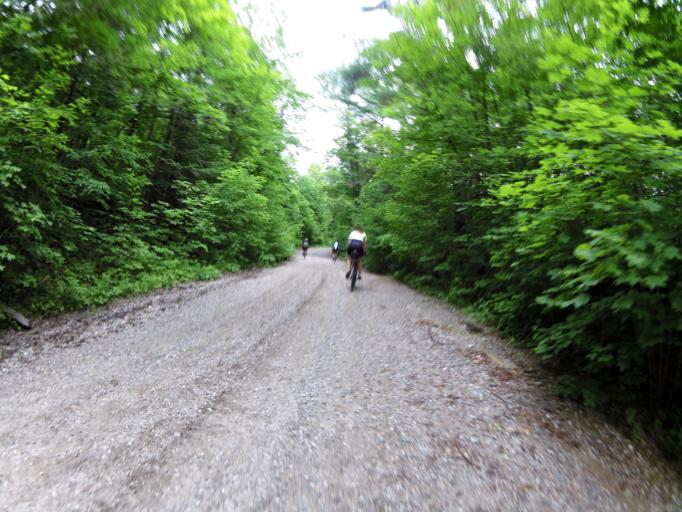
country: CA
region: Ontario
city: Perth
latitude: 45.0267
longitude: -76.5630
